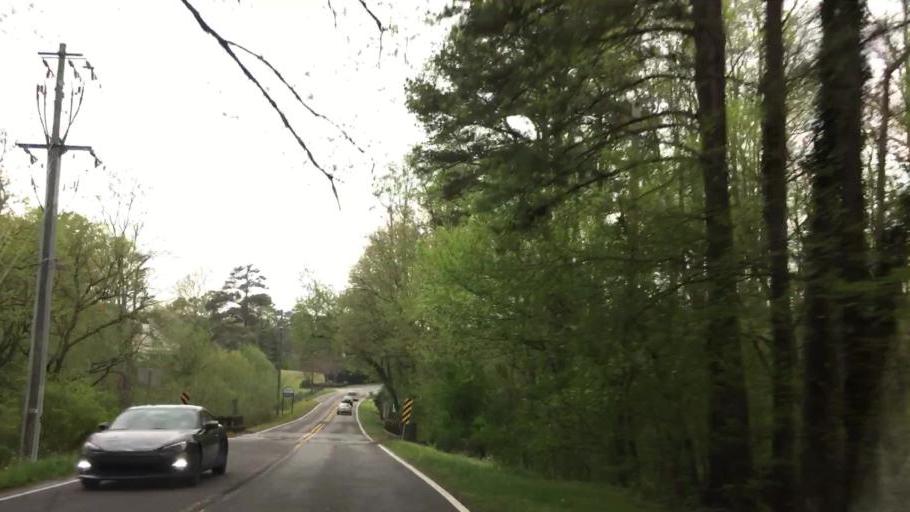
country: US
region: Georgia
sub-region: Fulton County
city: Milton
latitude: 34.1783
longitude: -84.3380
